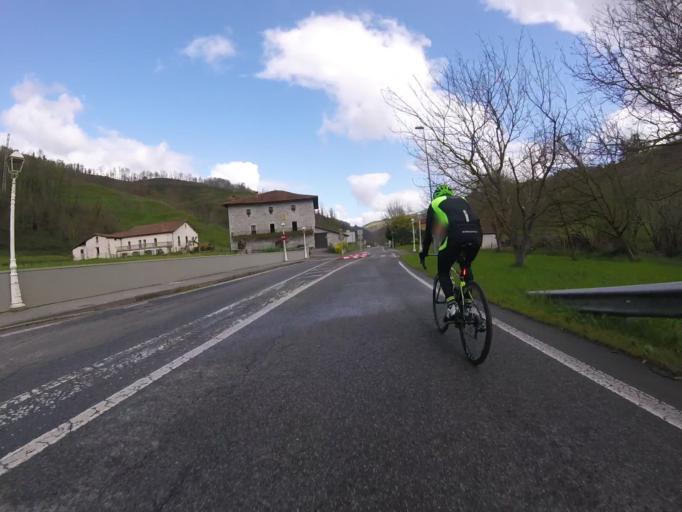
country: ES
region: Basque Country
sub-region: Provincia de Guipuzcoa
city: Amezqueta
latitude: 43.0538
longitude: -2.0888
